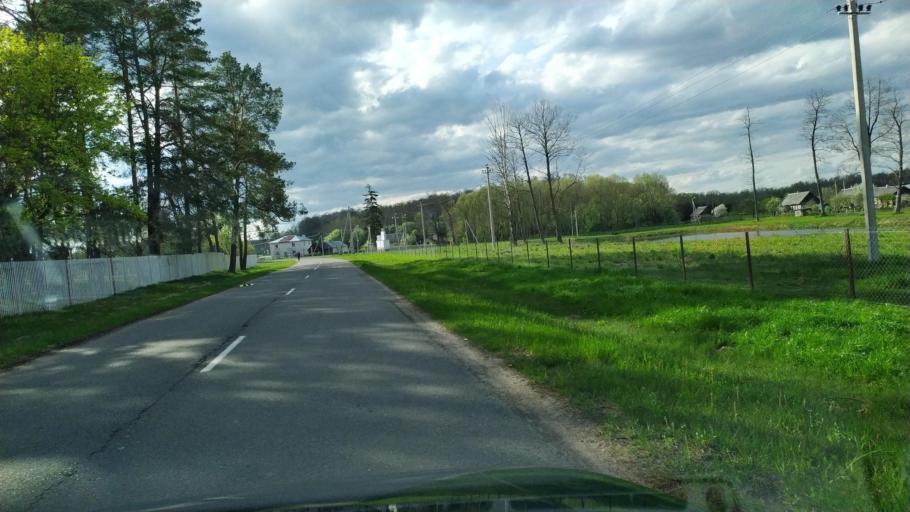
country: BY
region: Brest
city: Pruzhany
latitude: 52.6994
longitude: 24.2157
